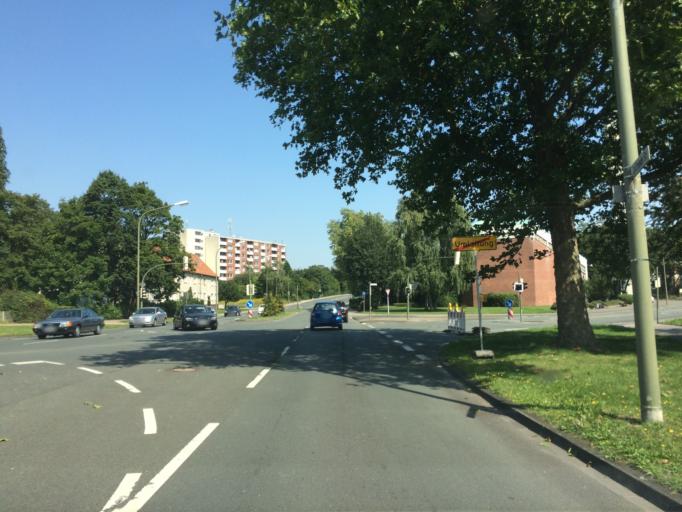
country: DE
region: North Rhine-Westphalia
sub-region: Regierungsbezirk Arnsberg
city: Hamm
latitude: 51.6682
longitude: 7.7726
